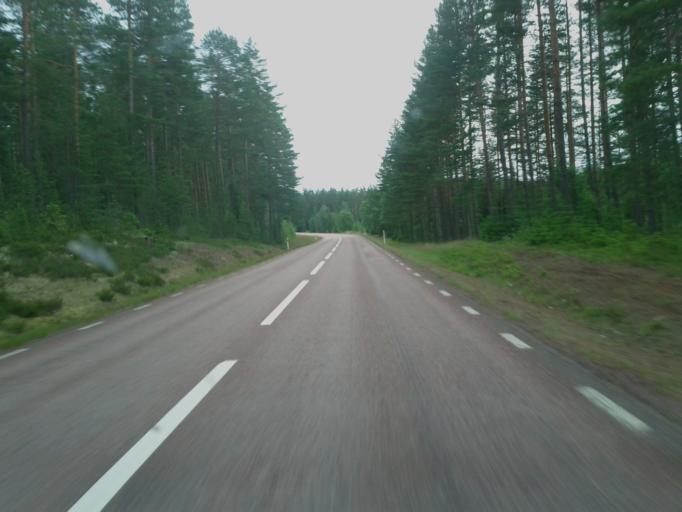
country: SE
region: Dalarna
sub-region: Mora Kommun
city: Mora
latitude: 61.0928
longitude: 14.3030
